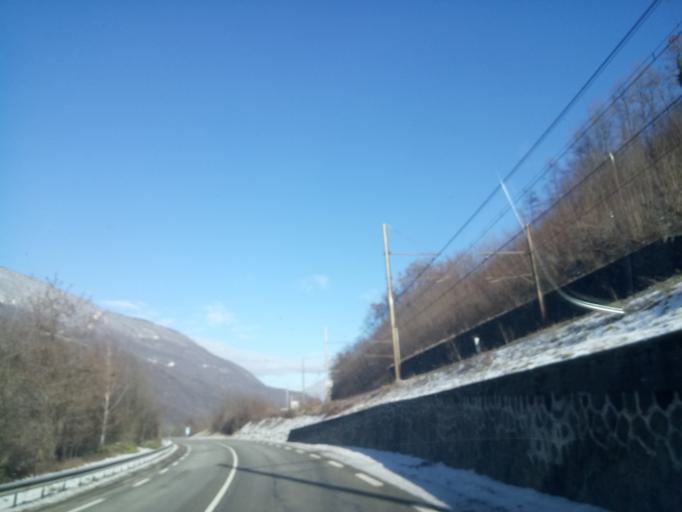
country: FR
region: Rhone-Alpes
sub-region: Departement de la Savoie
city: Saint-Remy-de-Maurienne
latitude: 45.4296
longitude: 6.2794
